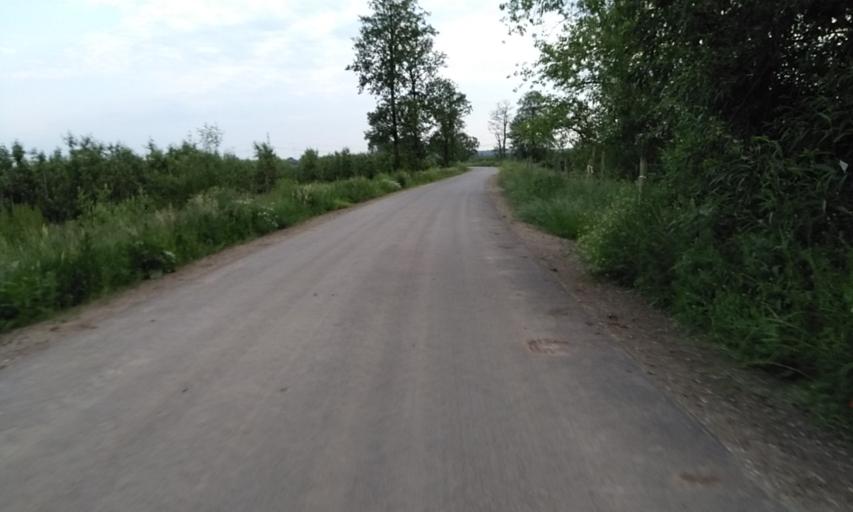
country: DE
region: Lower Saxony
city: Mittelnkirchen
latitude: 53.5152
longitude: 9.6368
